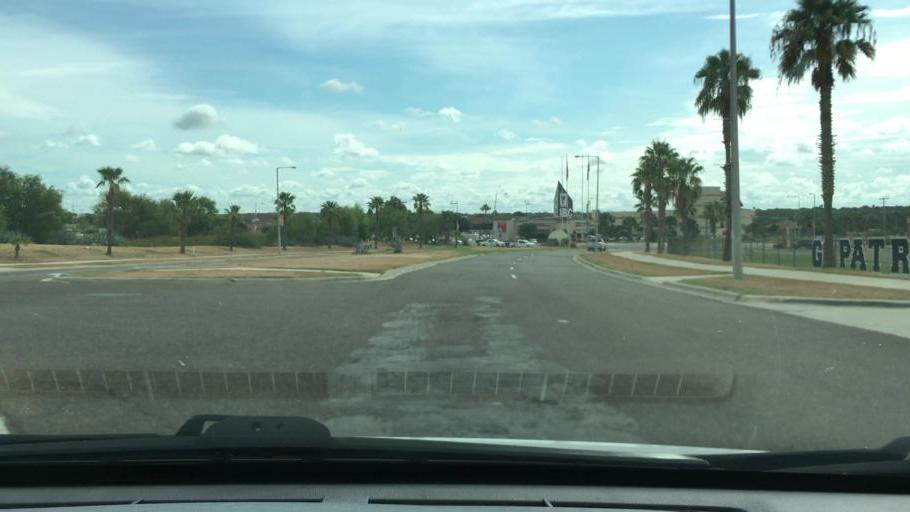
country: US
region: Texas
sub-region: Webb County
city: Laredo
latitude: 27.6043
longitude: -99.4789
